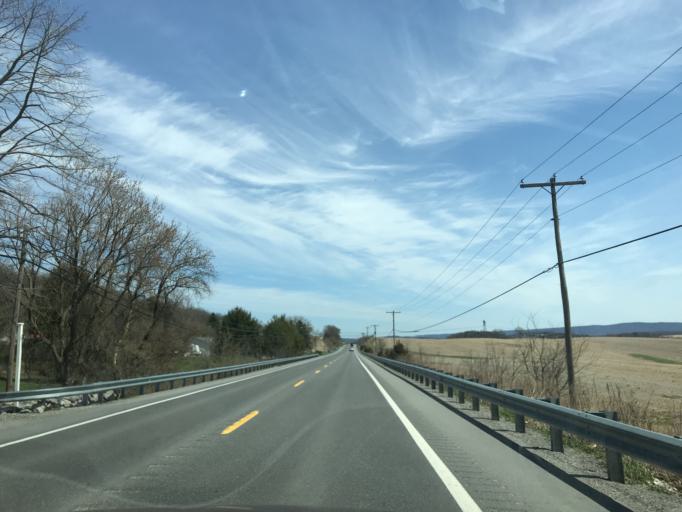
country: US
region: Pennsylvania
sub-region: Snyder County
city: Selinsgrove
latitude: 40.8068
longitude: -76.9447
